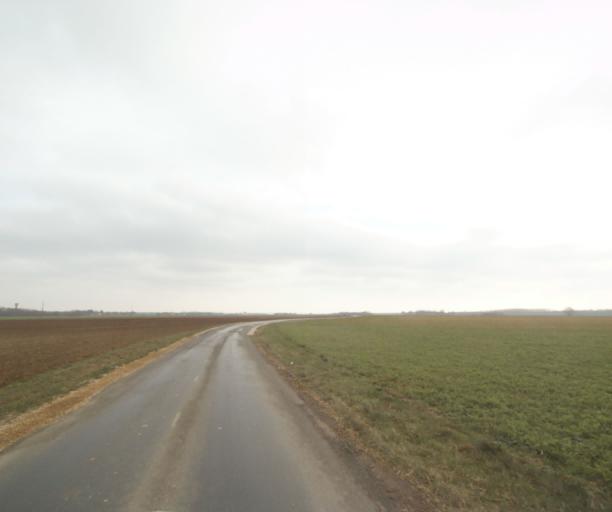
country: FR
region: Champagne-Ardenne
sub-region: Departement de la Haute-Marne
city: Villiers-en-Lieu
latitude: 48.6803
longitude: 4.8482
